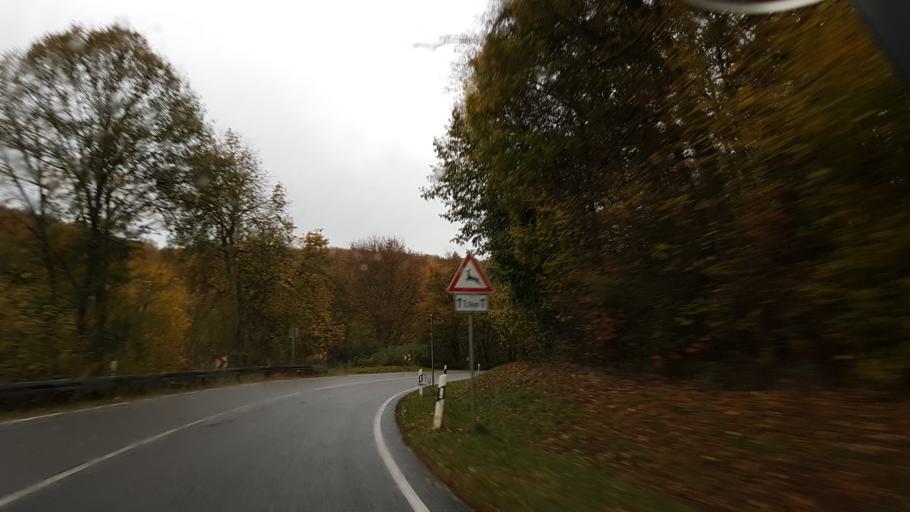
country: DE
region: Saarland
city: Hangard
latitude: 49.3946
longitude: 7.2168
